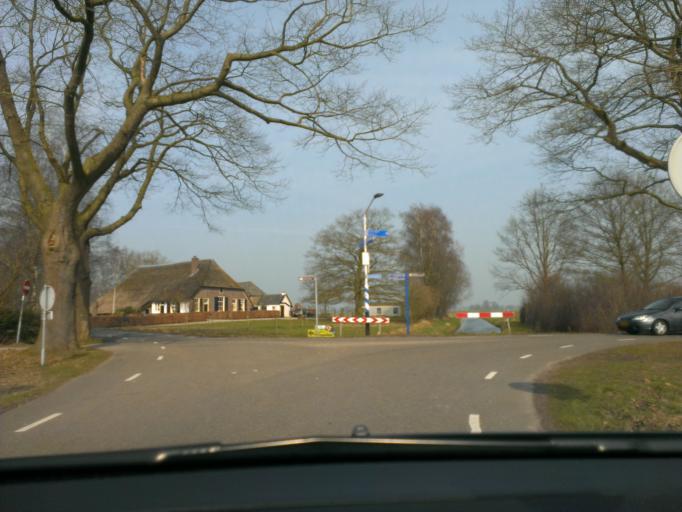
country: NL
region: Gelderland
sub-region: Gemeente Voorst
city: Twello
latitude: 52.2477
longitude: 6.0540
